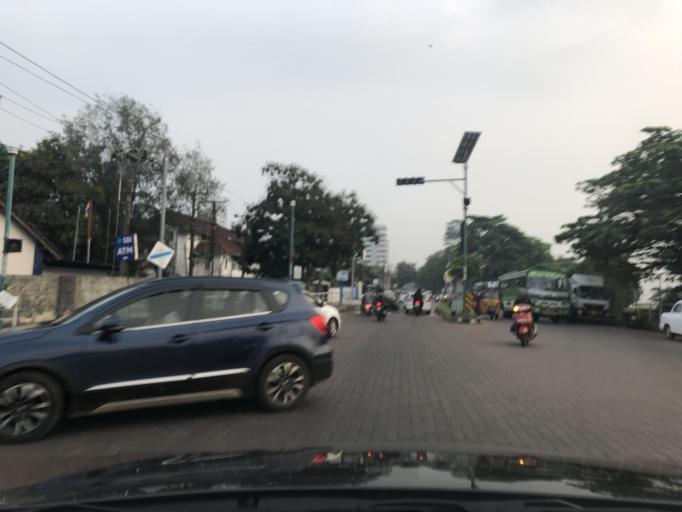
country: IN
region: Kerala
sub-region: Kozhikode
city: Kozhikode
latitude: 11.2635
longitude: 75.7679
